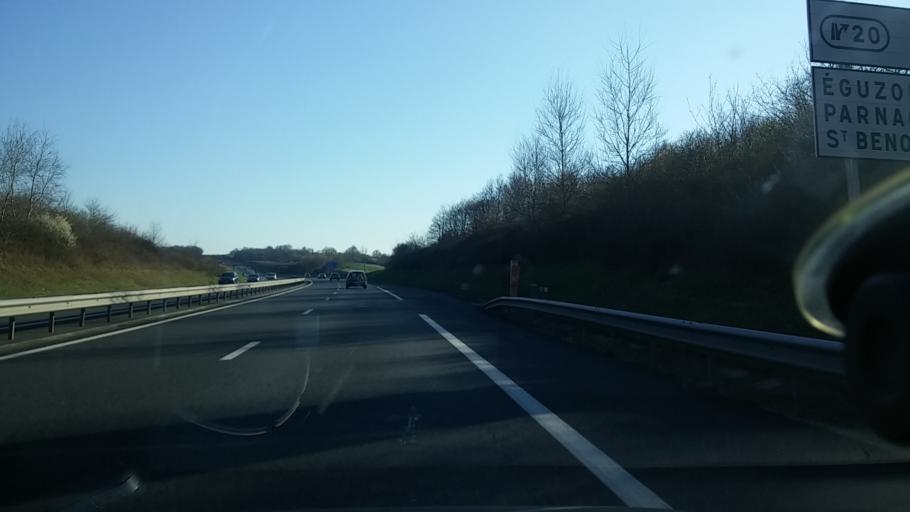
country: FR
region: Centre
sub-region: Departement de l'Indre
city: Le Pechereau
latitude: 46.5011
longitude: 1.4999
